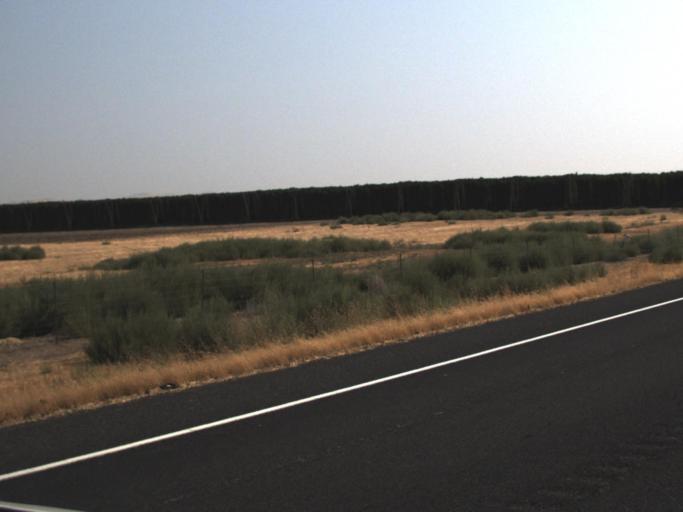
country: US
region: Washington
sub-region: Yakima County
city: Zillah
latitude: 46.5291
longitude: -120.2683
